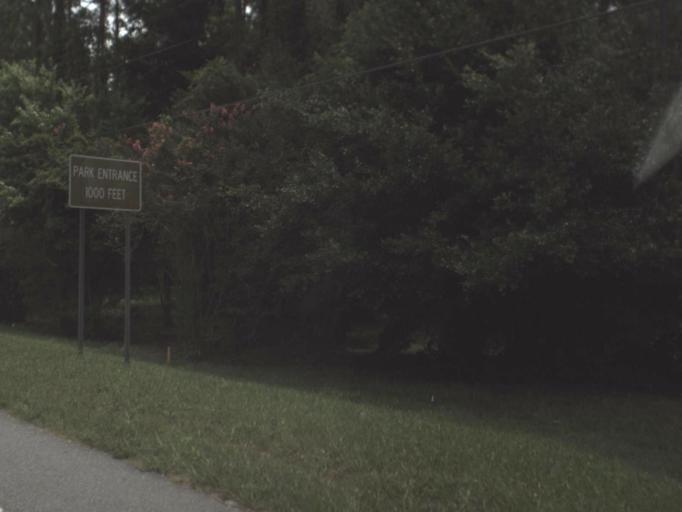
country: US
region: Florida
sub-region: Pasco County
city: Dade City
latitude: 28.3471
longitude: -82.2143
